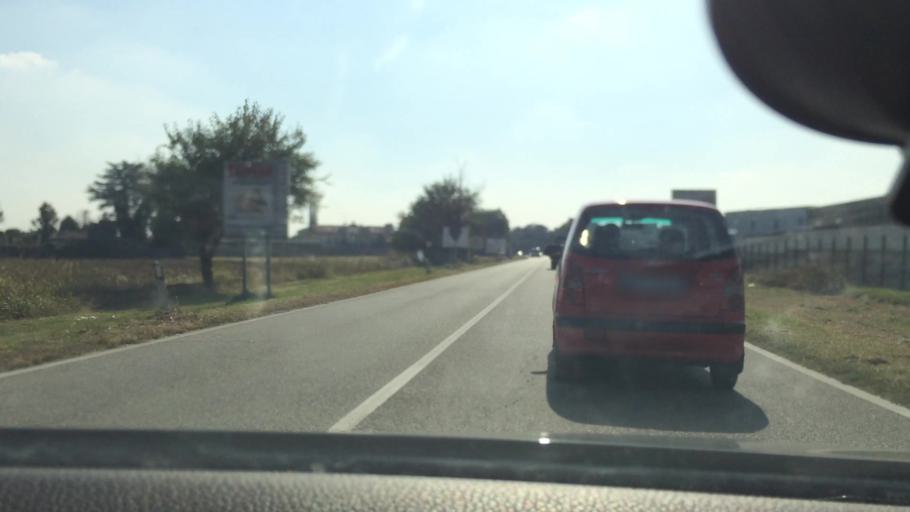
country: IT
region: Lombardy
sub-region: Citta metropolitana di Milano
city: Mesero
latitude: 45.5058
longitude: 8.8583
